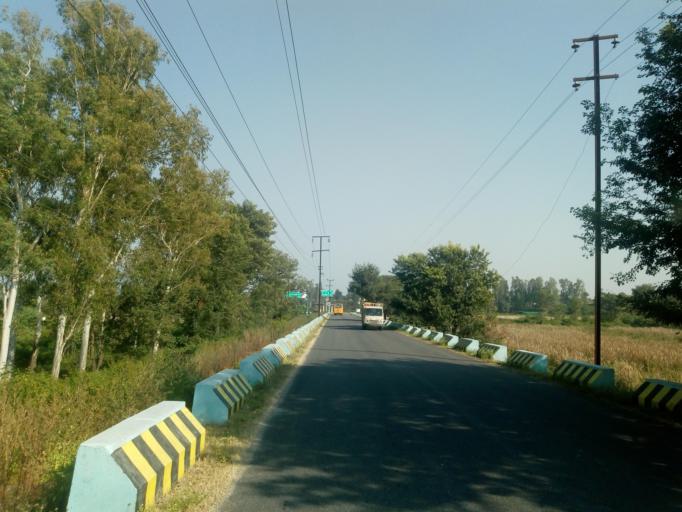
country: IN
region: Himachal Pradesh
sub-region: Sirmaur
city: Paonta Sahib
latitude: 30.4421
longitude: 77.6752
